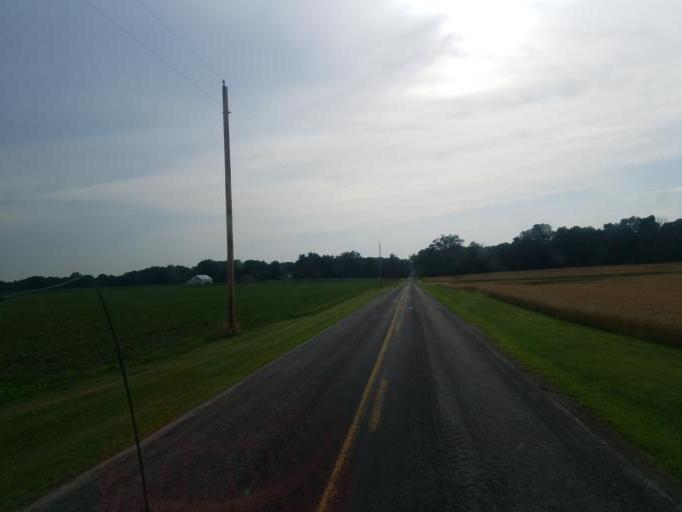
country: US
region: Ohio
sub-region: Wayne County
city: West Salem
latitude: 40.9009
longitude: -82.1286
